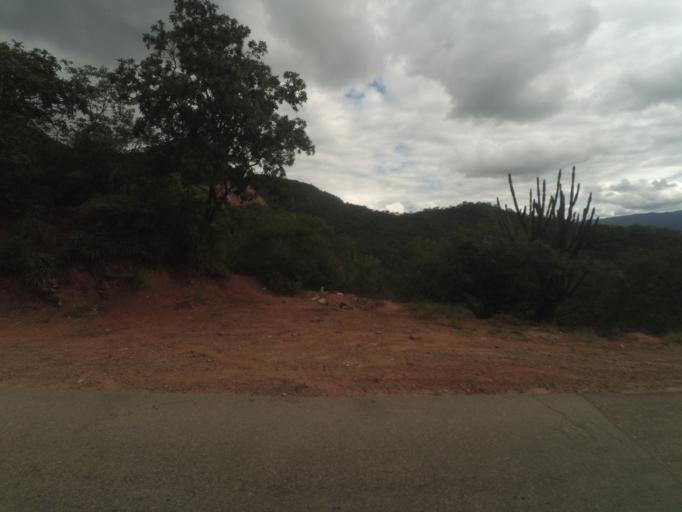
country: BO
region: Santa Cruz
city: Samaipata
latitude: -18.1654
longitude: -63.9041
